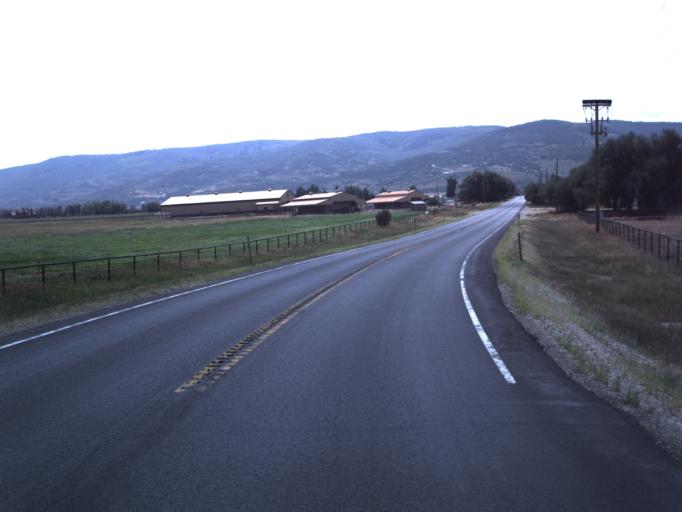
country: US
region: Utah
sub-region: Summit County
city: Francis
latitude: 40.5958
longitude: -111.2424
